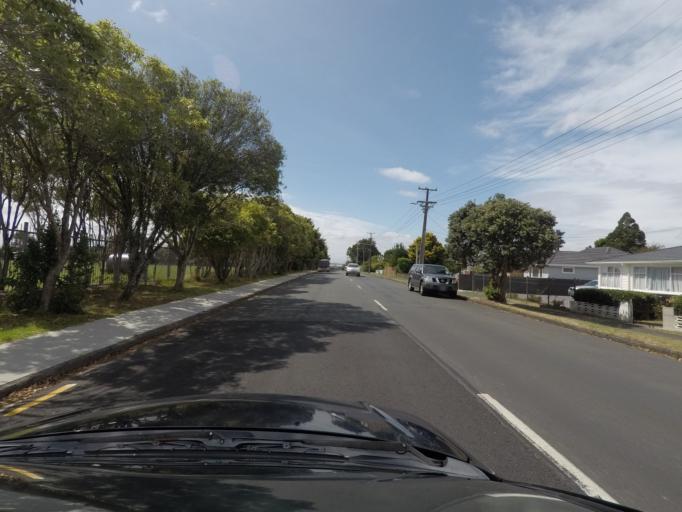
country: NZ
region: Auckland
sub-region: Auckland
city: Waitakere
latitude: -36.8987
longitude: 174.6672
